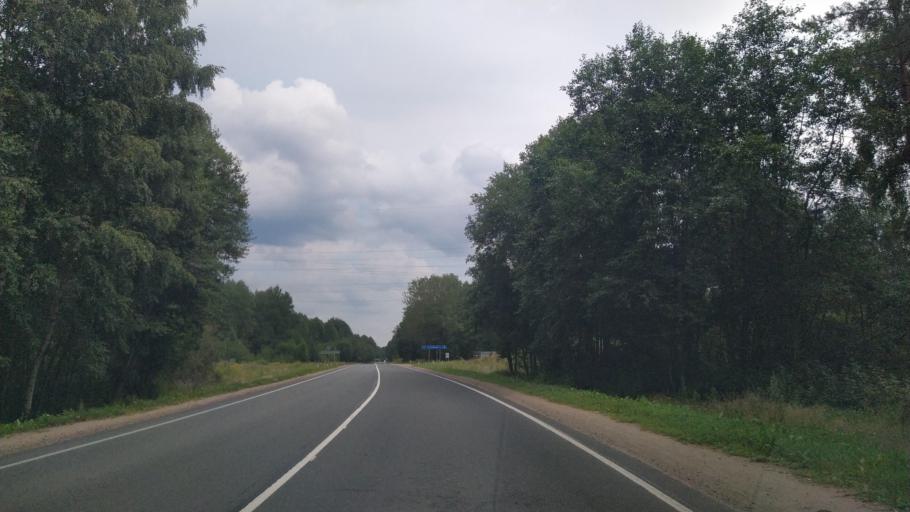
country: RU
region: Pskov
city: Pskov
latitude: 57.8336
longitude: 28.5179
